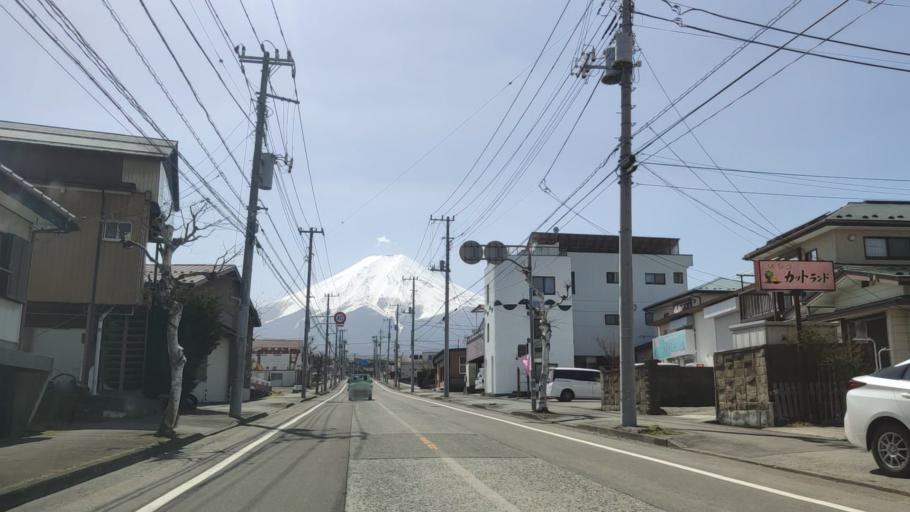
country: JP
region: Yamanashi
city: Fujikawaguchiko
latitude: 35.4736
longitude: 138.7991
